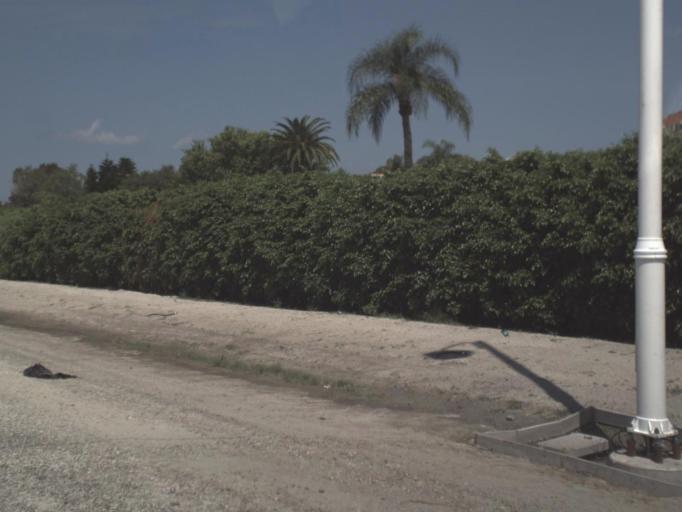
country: US
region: Florida
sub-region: Pinellas County
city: Tierra Verde
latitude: 27.7106
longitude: -82.7192
